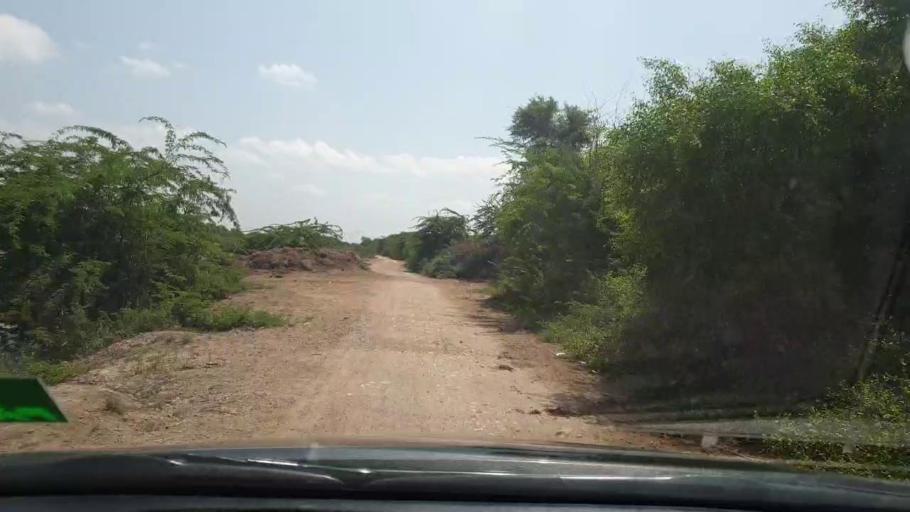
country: PK
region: Sindh
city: Tando Bago
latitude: 24.8544
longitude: 69.0893
